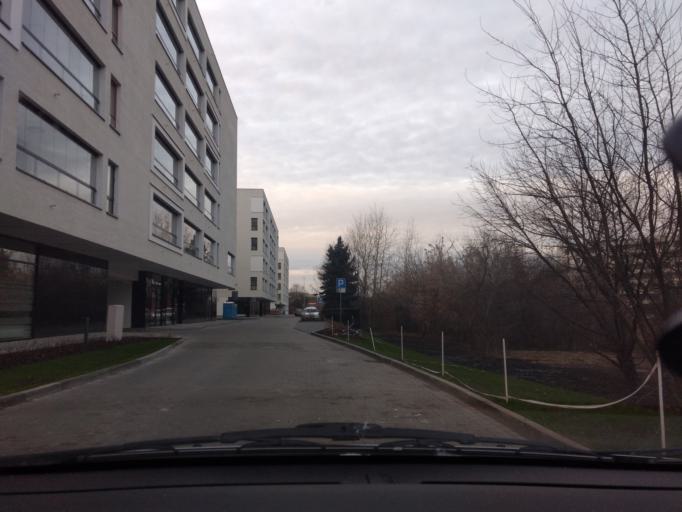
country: PL
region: Masovian Voivodeship
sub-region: Warszawa
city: Praga Poludnie
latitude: 52.2282
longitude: 21.0744
